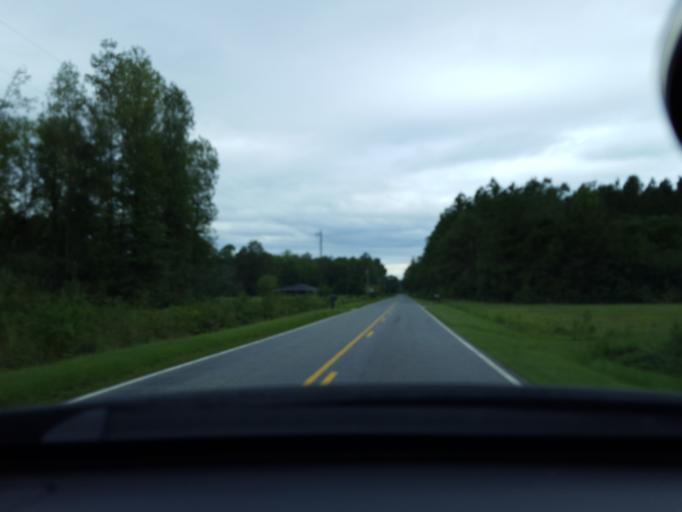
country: US
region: North Carolina
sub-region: Sampson County
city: Clinton
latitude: 34.7781
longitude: -78.3557
